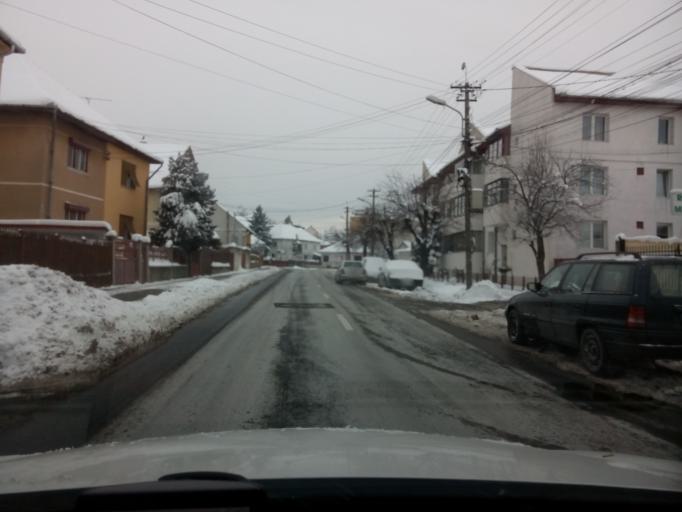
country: RO
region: Sibiu
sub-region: Municipiul Sibiu
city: Sibiu
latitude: 45.7948
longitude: 24.1403
